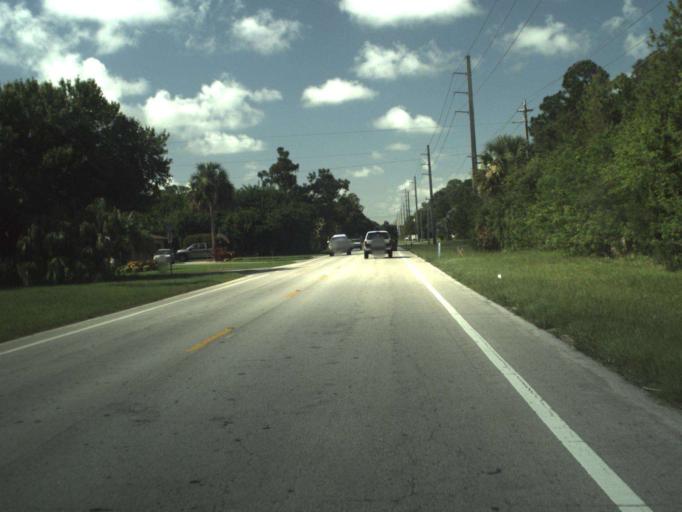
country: US
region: Florida
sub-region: Indian River County
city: Gifford
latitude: 27.6795
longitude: -80.4463
